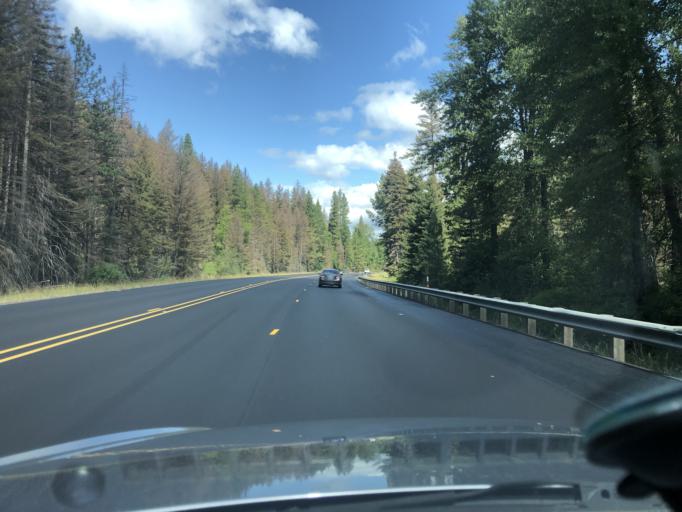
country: US
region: Washington
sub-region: Kittitas County
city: Cle Elum
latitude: 47.2747
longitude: -120.6983
